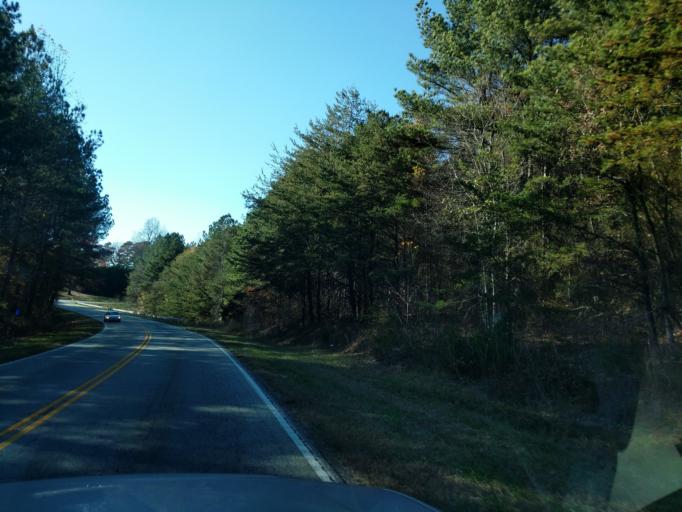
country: US
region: South Carolina
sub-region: Spartanburg County
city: Landrum
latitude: 35.1273
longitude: -82.1332
